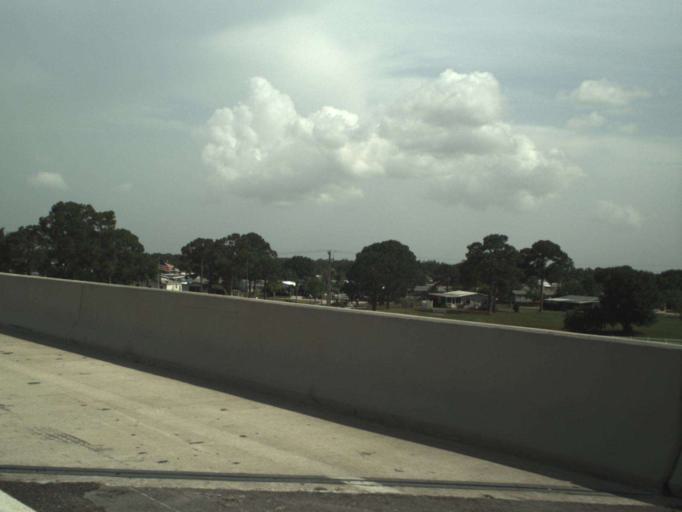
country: US
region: Florida
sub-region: Saint Lucie County
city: Lakewood Park
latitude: 27.4706
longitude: -80.4281
